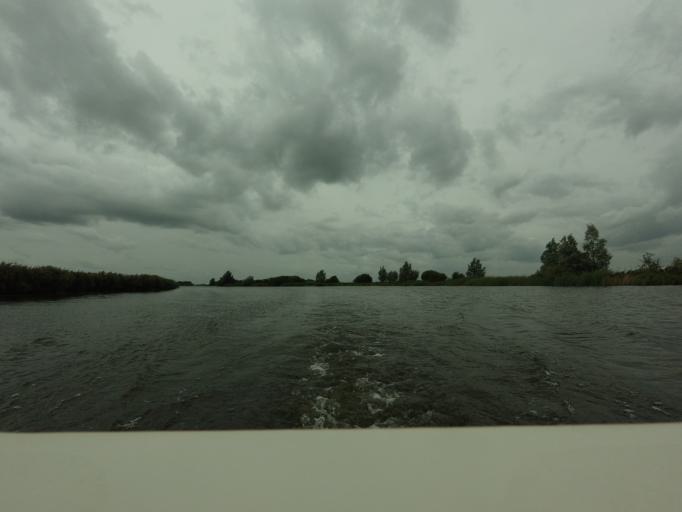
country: NL
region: Friesland
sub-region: Gemeente Boarnsterhim
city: Aldeboarn
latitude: 53.1000
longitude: 5.9161
